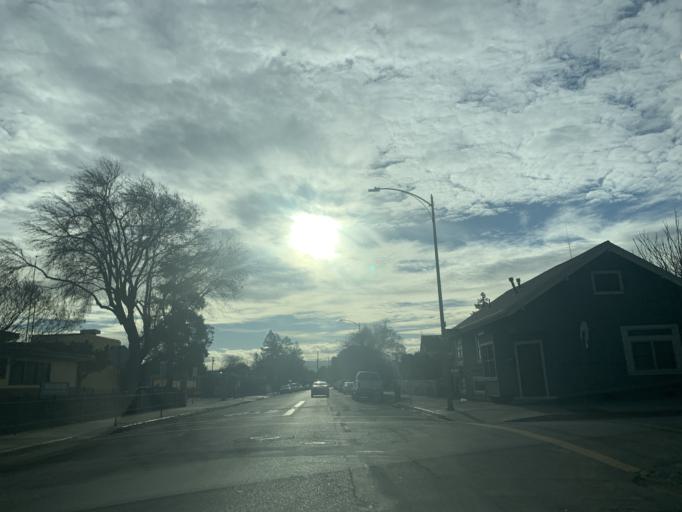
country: US
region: California
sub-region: Santa Clara County
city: San Jose
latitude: 37.3218
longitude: -121.8817
